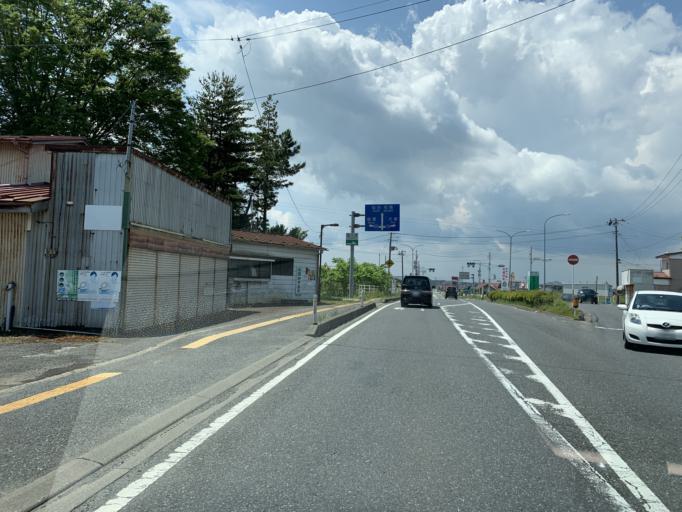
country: JP
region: Miyagi
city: Wakuya
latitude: 38.4663
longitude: 141.0937
